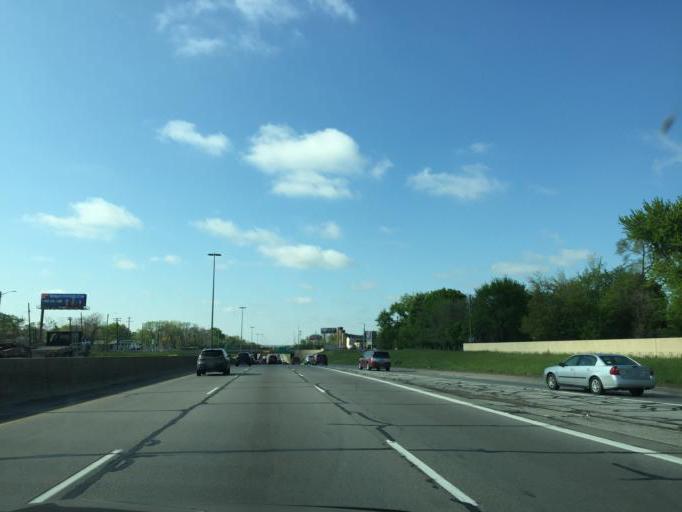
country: US
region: Michigan
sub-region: Wayne County
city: Dearborn
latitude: 42.3748
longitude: -83.2169
